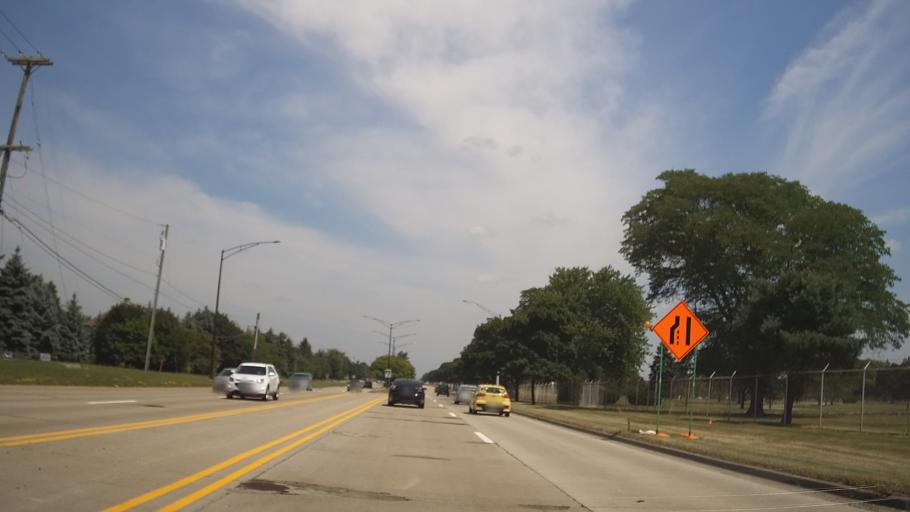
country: US
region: Michigan
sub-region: Oakland County
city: Troy
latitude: 42.5830
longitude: -83.1683
